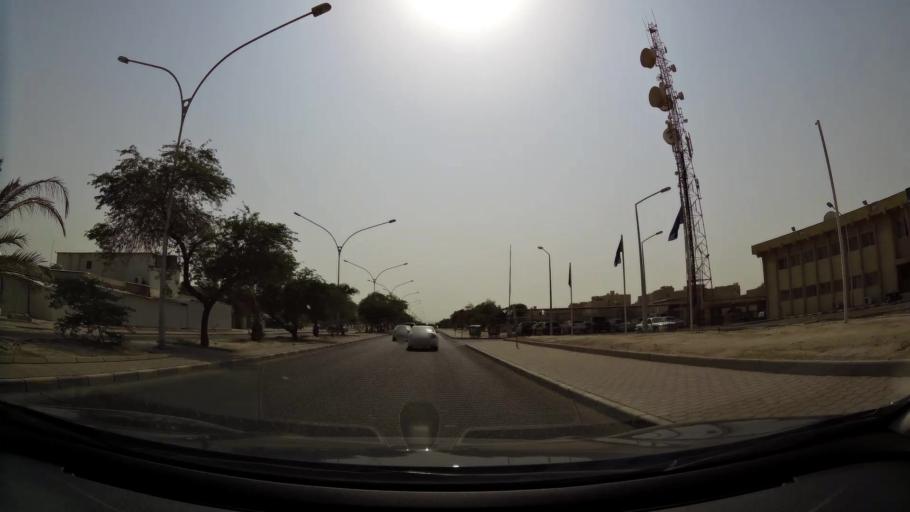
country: KW
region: Muhafazat al Jahra'
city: Al Jahra'
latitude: 29.3257
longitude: 47.6805
